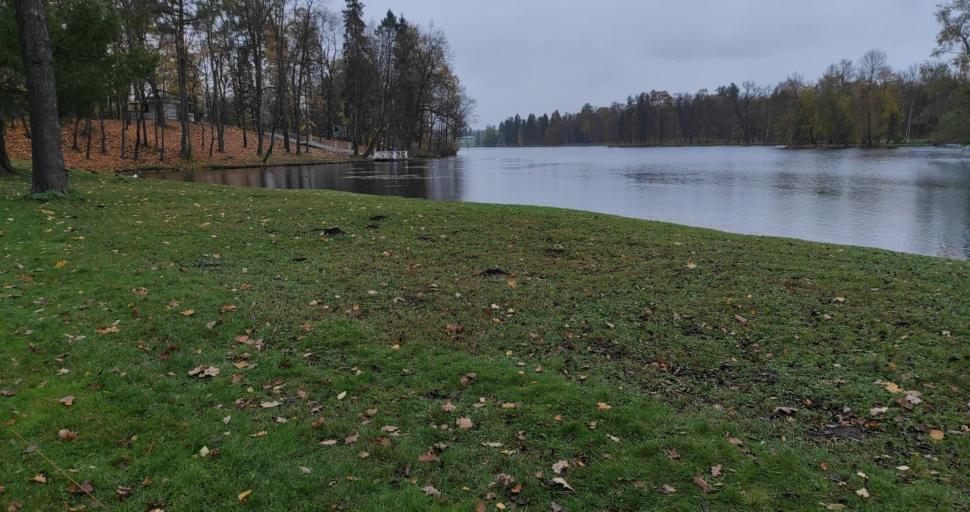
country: RU
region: Leningrad
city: Gatchina
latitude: 59.5634
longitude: 30.1134
